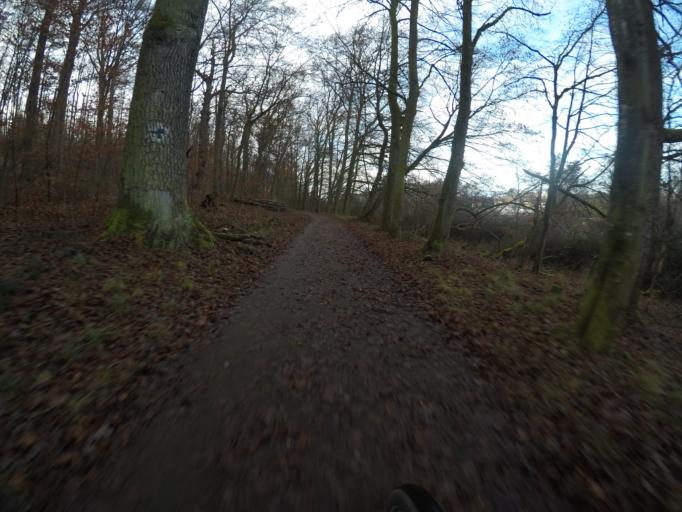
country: DE
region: Baden-Wuerttemberg
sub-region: Regierungsbezirk Stuttgart
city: Sindelfingen
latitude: 48.7204
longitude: 9.0156
